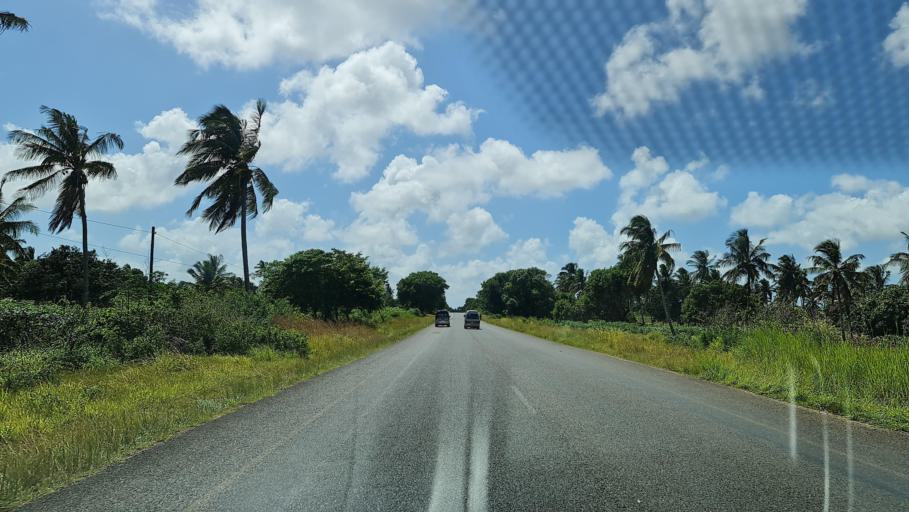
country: MZ
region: Inhambane
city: Maxixe
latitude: -24.5408
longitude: 34.9206
